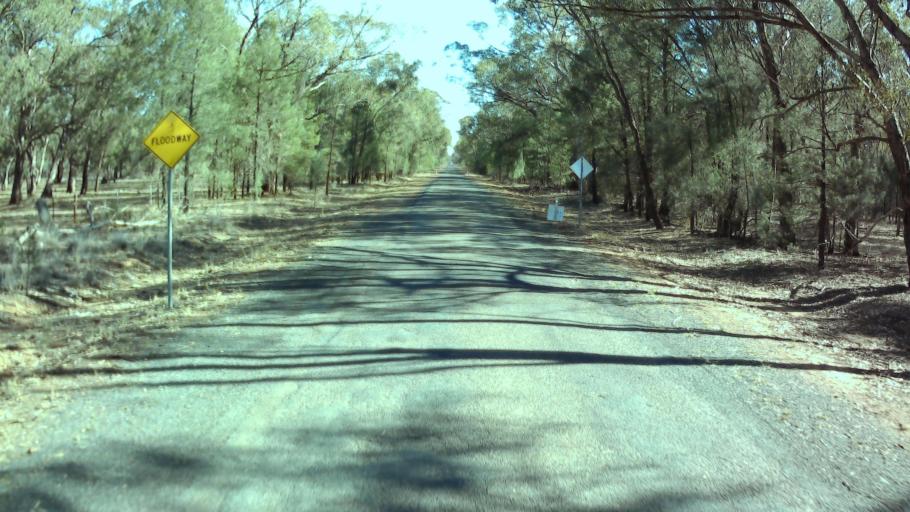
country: AU
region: New South Wales
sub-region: Weddin
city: Grenfell
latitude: -33.8142
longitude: 147.9534
